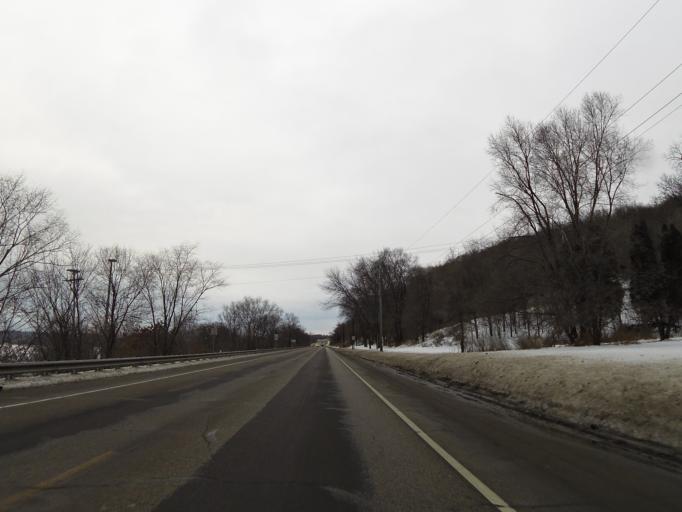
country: US
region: Minnesota
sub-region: Washington County
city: Bayport
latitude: 45.0015
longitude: -92.7788
